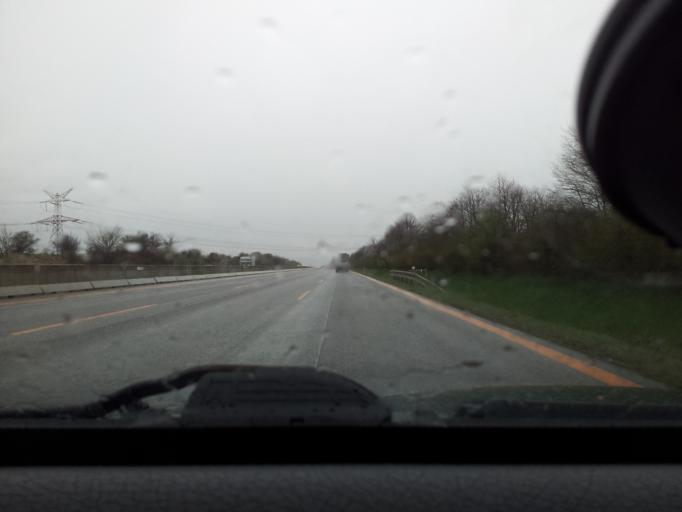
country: SK
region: Bratislavsky
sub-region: Okres Pezinok
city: Pezinok
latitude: 48.2149
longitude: 17.2920
